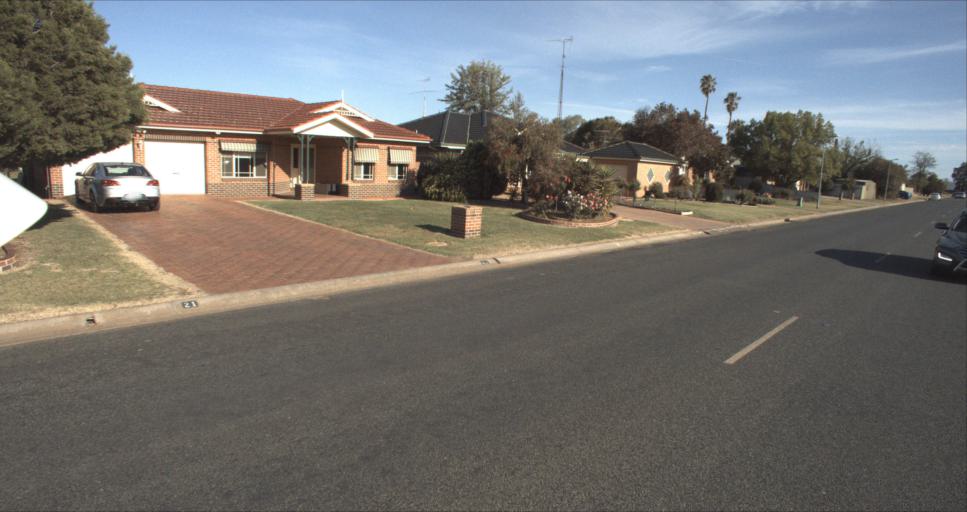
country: AU
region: New South Wales
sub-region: Leeton
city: Leeton
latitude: -34.5435
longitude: 146.3996
